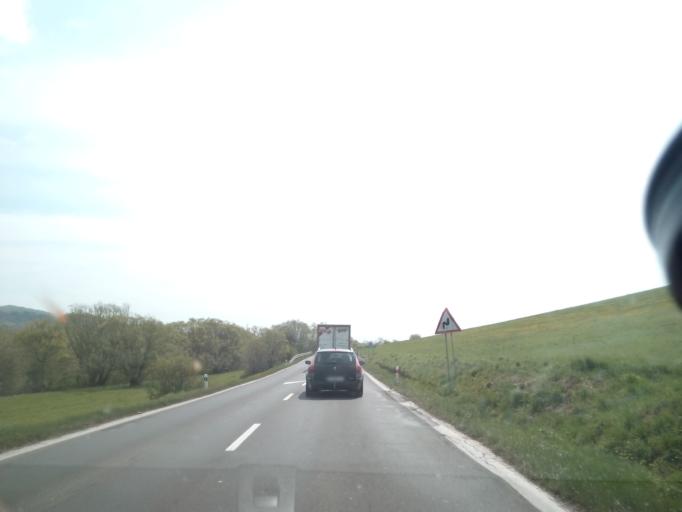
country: SK
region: Presovsky
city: Giraltovce
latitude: 49.0393
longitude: 21.4541
